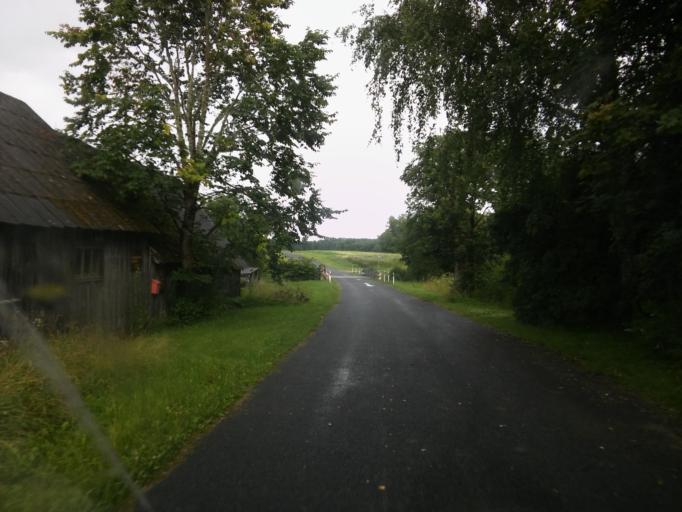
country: EE
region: Paernumaa
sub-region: Halinga vald
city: Parnu-Jaagupi
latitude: 58.7802
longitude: 24.5609
